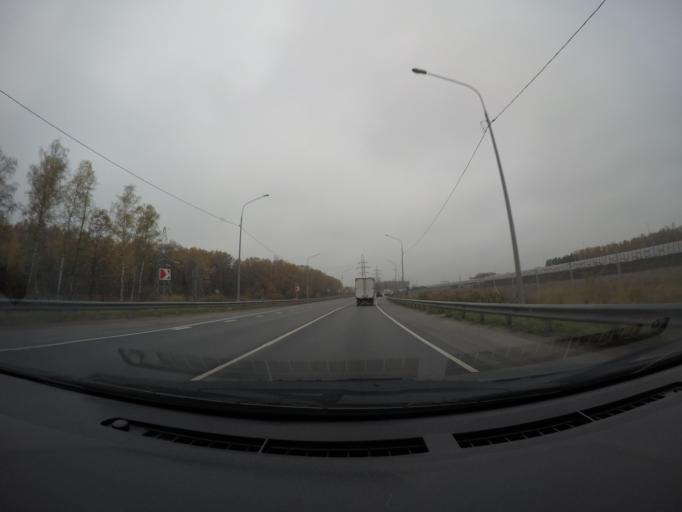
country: RU
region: Moskovskaya
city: Belyye Stolby
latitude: 55.3433
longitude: 37.8610
